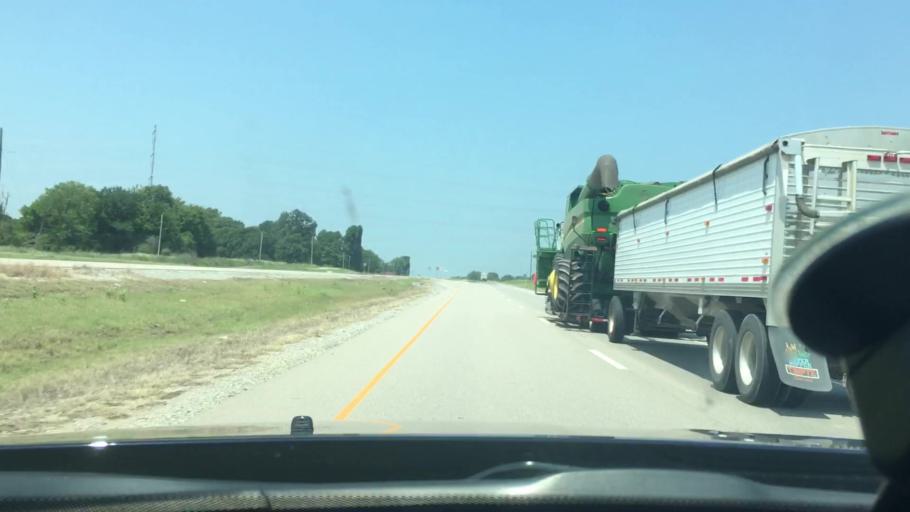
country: US
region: Oklahoma
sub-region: Atoka County
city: Atoka
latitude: 34.3294
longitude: -96.0481
